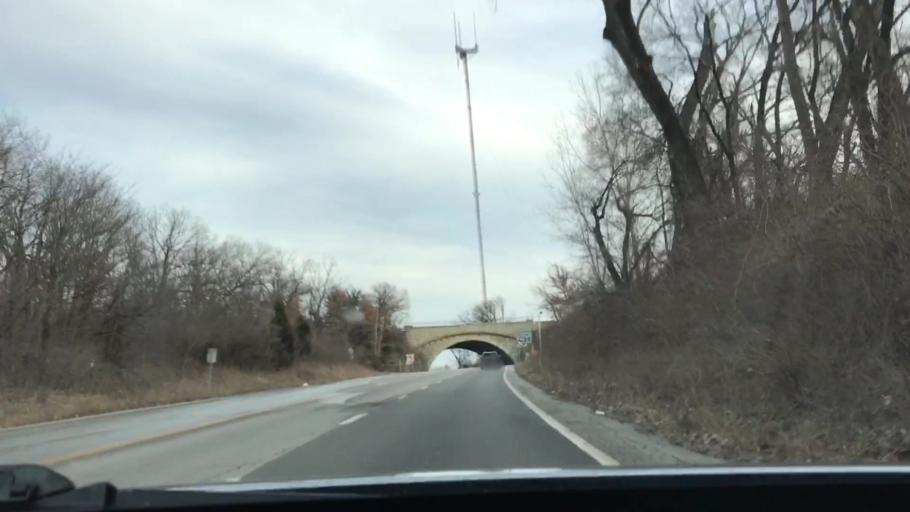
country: US
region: Missouri
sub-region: Jackson County
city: Sugar Creek
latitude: 39.0930
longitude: -94.4797
